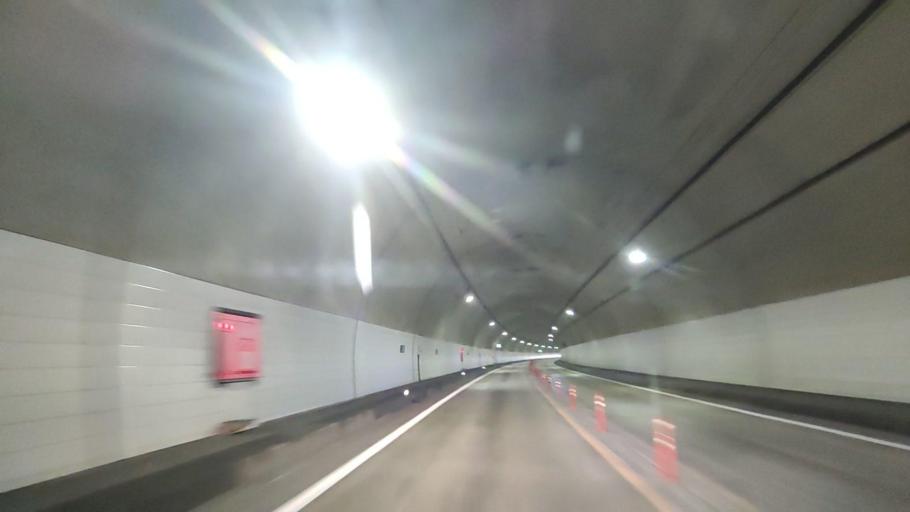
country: JP
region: Akita
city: Odate
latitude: 40.3620
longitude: 140.6953
